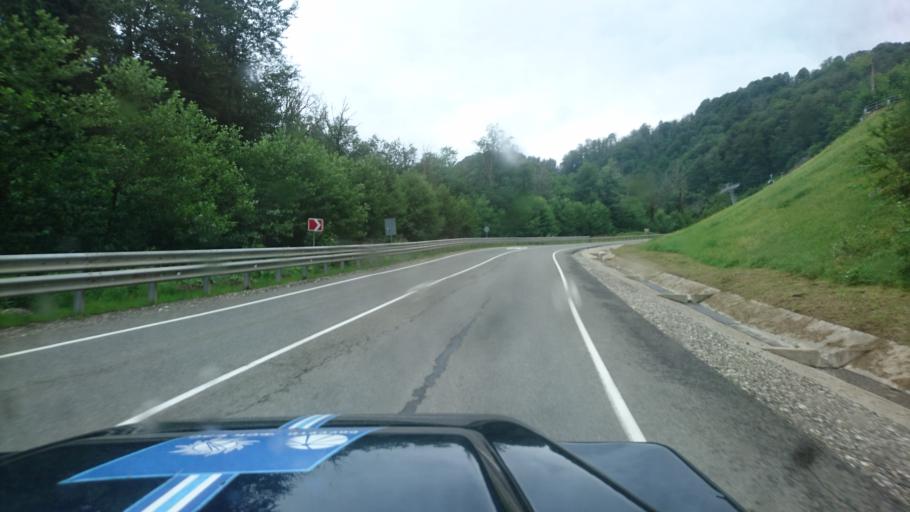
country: RU
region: Krasnodarskiy
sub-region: Sochi City
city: Krasnaya Polyana
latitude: 43.6682
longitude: 40.2904
